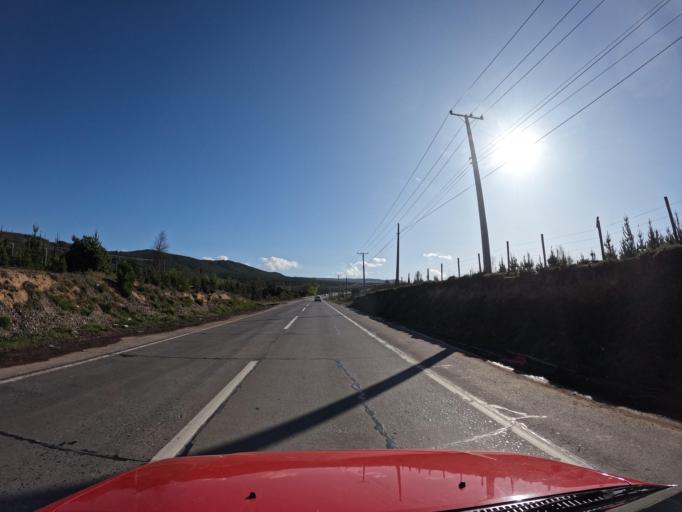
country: CL
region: Maule
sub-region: Provincia de Talca
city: Constitucion
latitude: -35.4460
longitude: -72.3099
